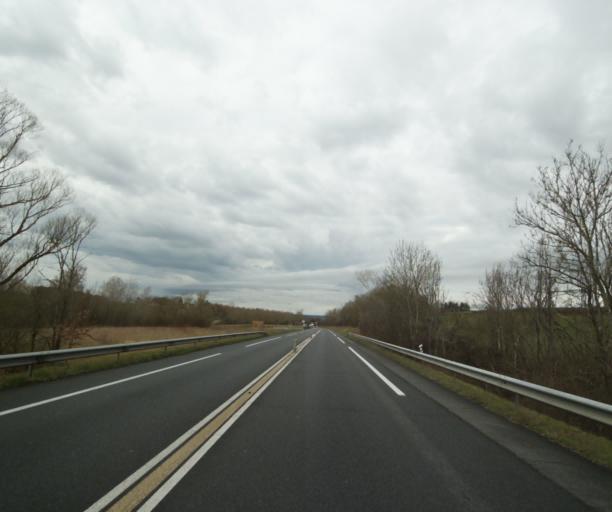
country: FR
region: Auvergne
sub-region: Departement de l'Allier
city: Toulon-sur-Allier
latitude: 46.4985
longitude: 3.3867
